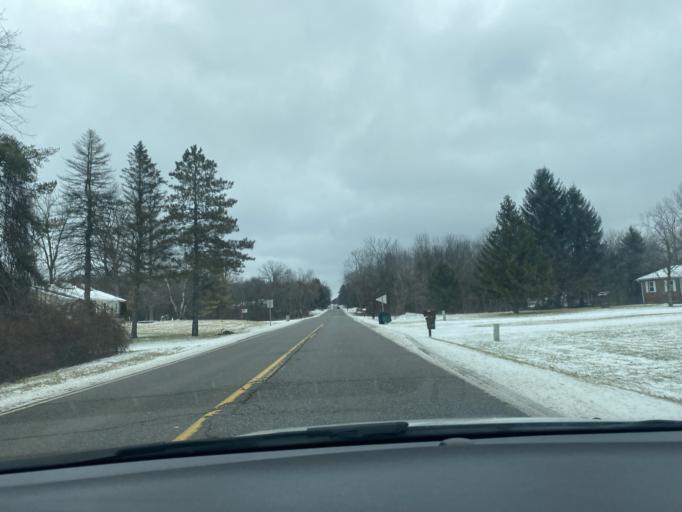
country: US
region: Michigan
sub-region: Lapeer County
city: Barnes Lake-Millers Lake
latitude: 43.2049
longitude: -83.3007
